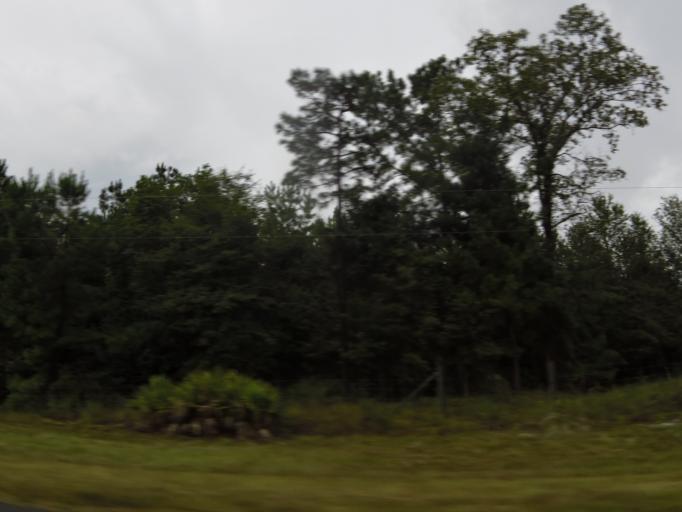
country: US
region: Florida
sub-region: Duval County
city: Baldwin
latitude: 30.5032
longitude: -82.0365
